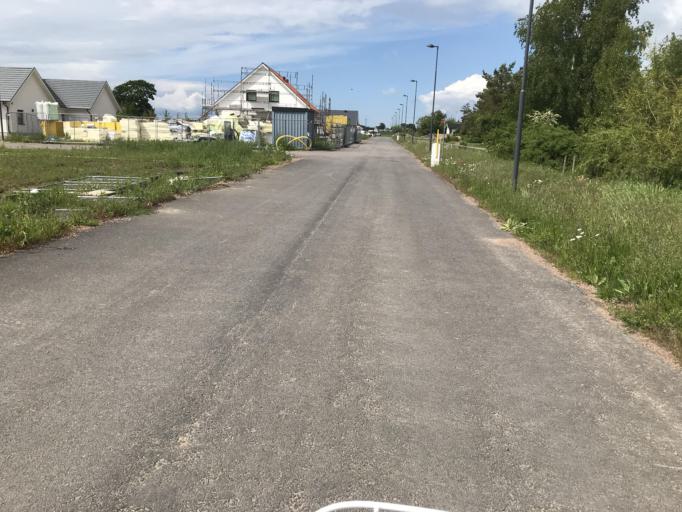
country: SE
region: Skane
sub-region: Landskrona
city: Landskrona
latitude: 55.8957
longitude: 12.8618
